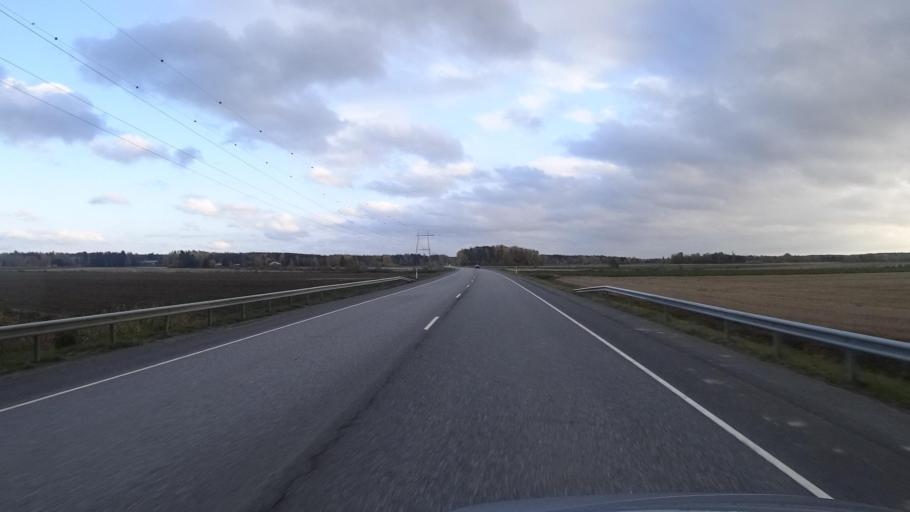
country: FI
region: Satakunta
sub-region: Rauma
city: Saekylae
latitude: 61.0306
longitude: 22.3947
